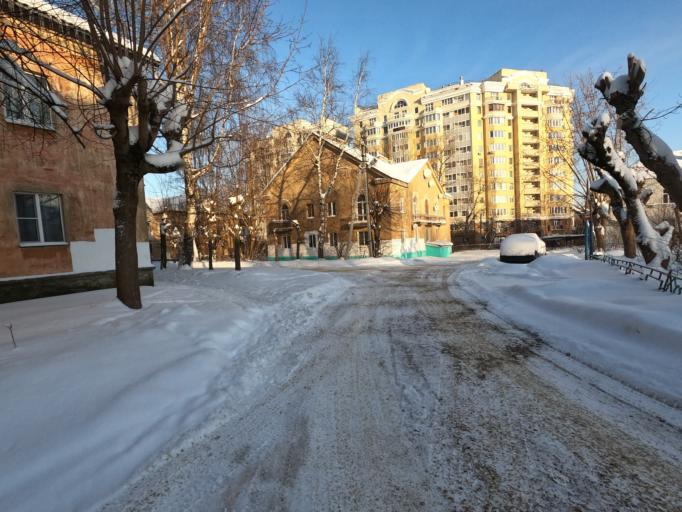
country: RU
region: Moskovskaya
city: Dmitrov
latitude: 56.3409
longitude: 37.5397
